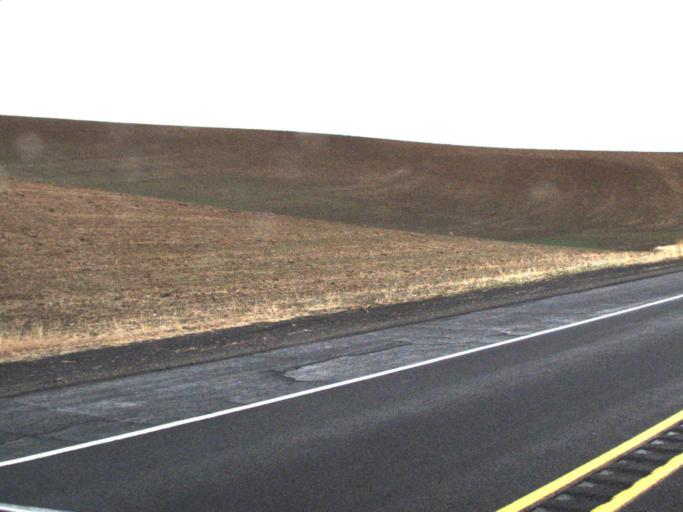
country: US
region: Washington
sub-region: Whitman County
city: Pullman
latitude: 46.7128
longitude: -117.2173
